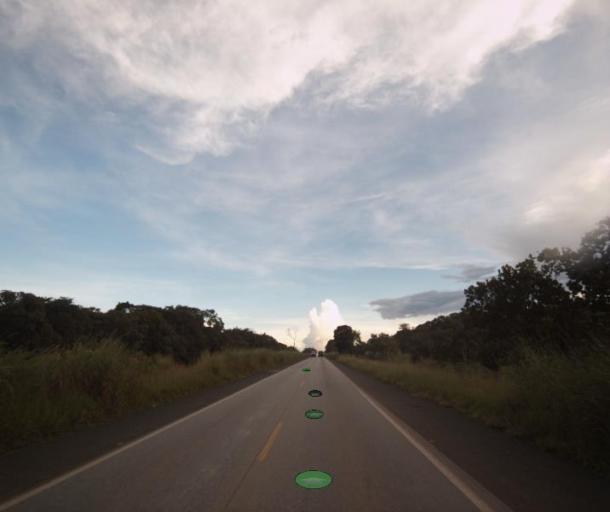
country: BR
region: Goias
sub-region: Uruacu
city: Uruacu
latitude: -14.2042
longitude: -49.1297
